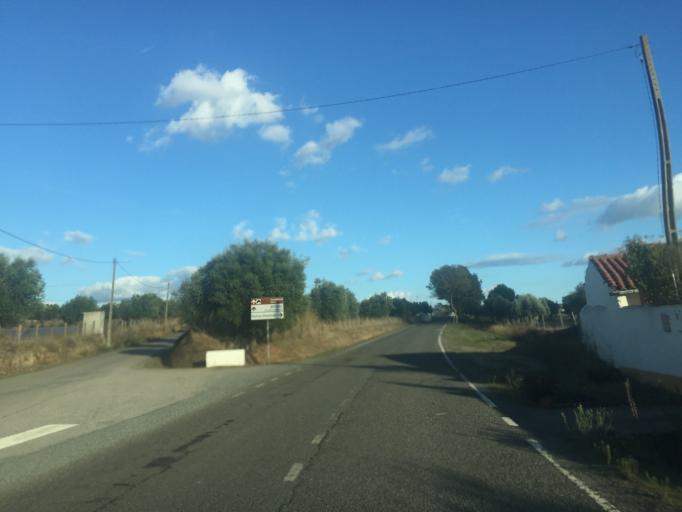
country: PT
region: Portalegre
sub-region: Alter do Chao
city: Alter do Chao
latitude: 39.1965
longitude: -7.6704
